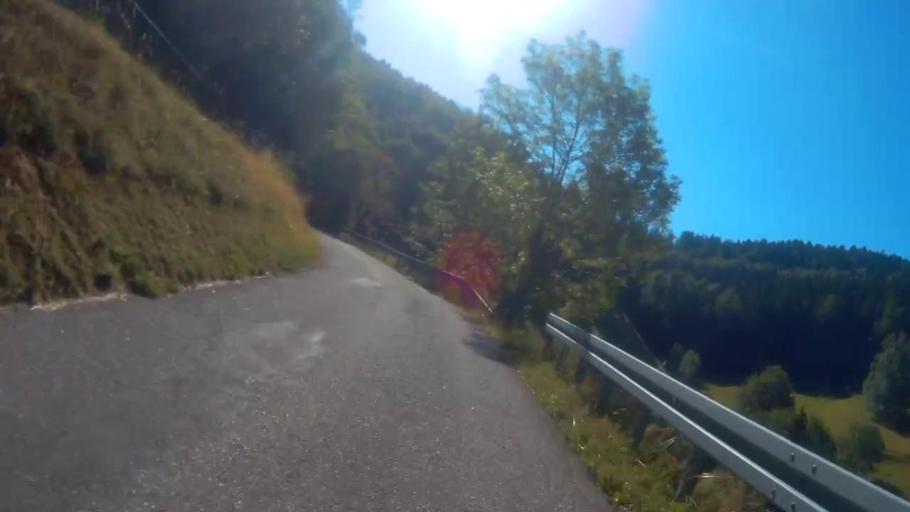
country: DE
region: Baden-Wuerttemberg
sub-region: Freiburg Region
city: Tunau
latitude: 47.7542
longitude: 7.9196
